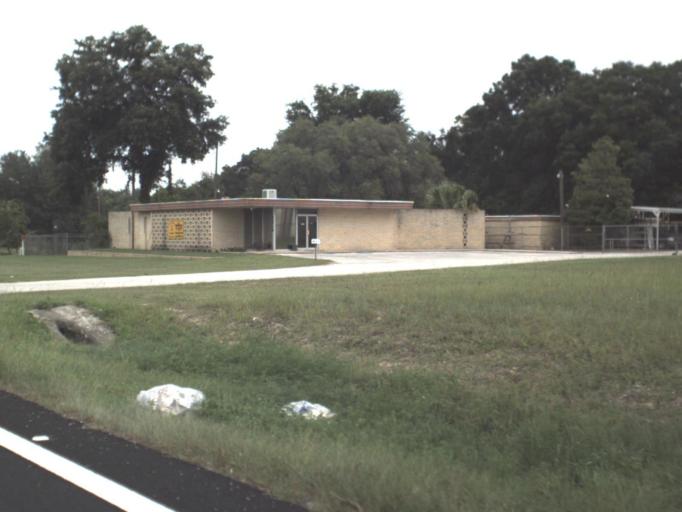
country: US
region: Florida
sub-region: Pasco County
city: Lacoochee
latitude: 28.4597
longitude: -82.1846
